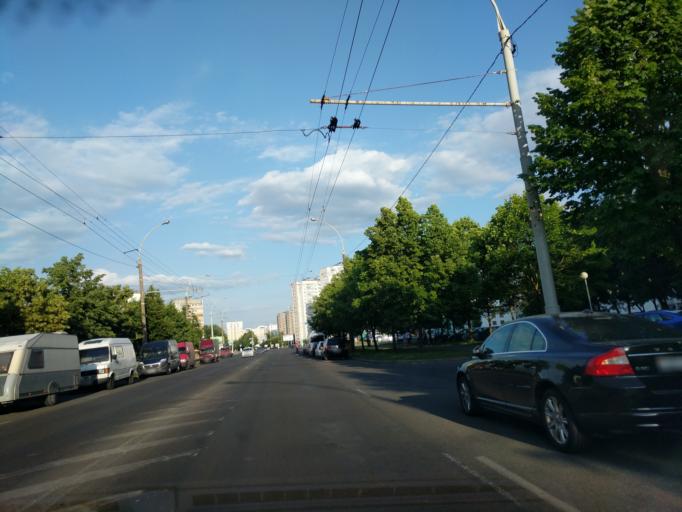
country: BY
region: Minsk
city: Malinovka
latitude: 53.8511
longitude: 27.4541
